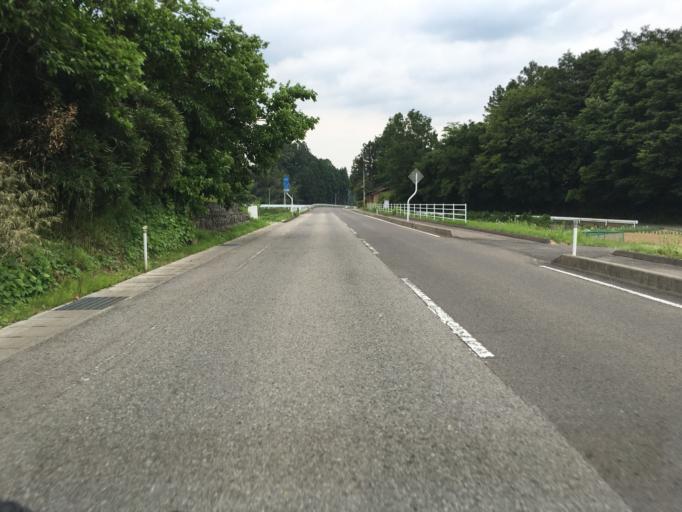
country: JP
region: Fukushima
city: Nihommatsu
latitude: 37.6399
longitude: 140.5357
